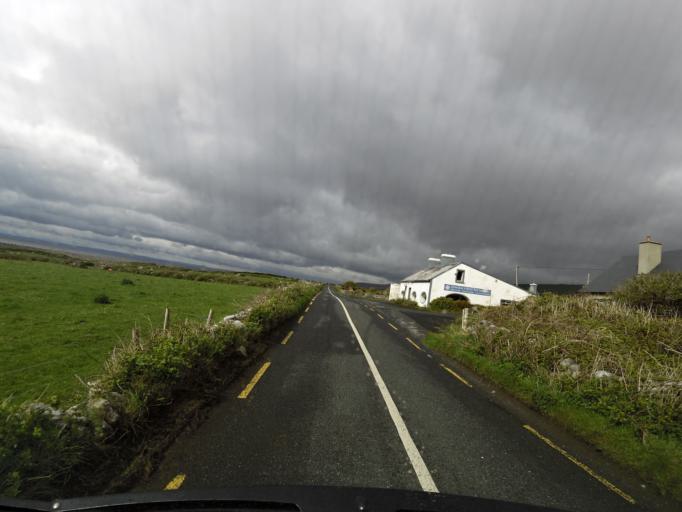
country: IE
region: Connaught
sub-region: County Galway
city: Bearna
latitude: 53.0943
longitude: -9.3058
